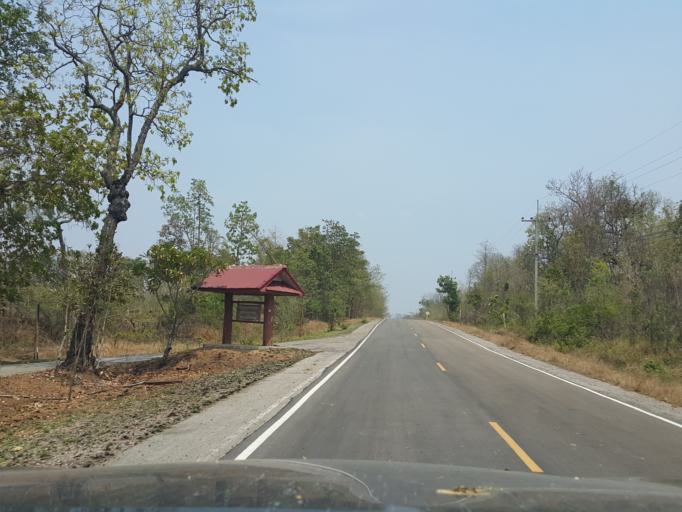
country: TH
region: Lampang
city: Mae Phrik
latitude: 17.5586
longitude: 99.1006
